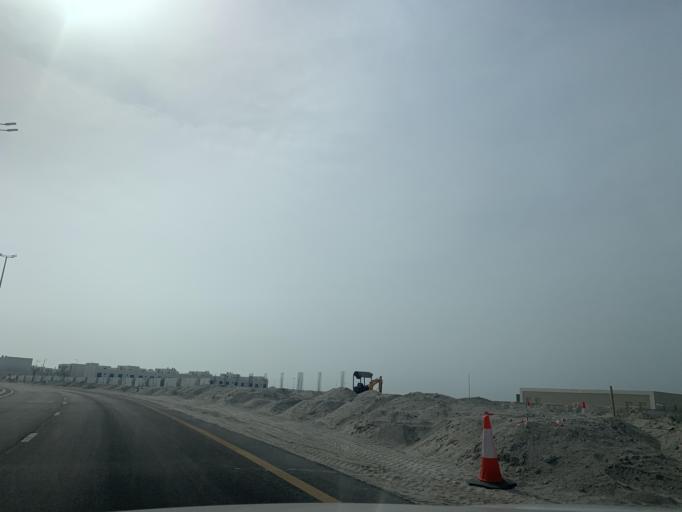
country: BH
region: Muharraq
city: Al Muharraq
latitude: 26.3129
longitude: 50.6398
